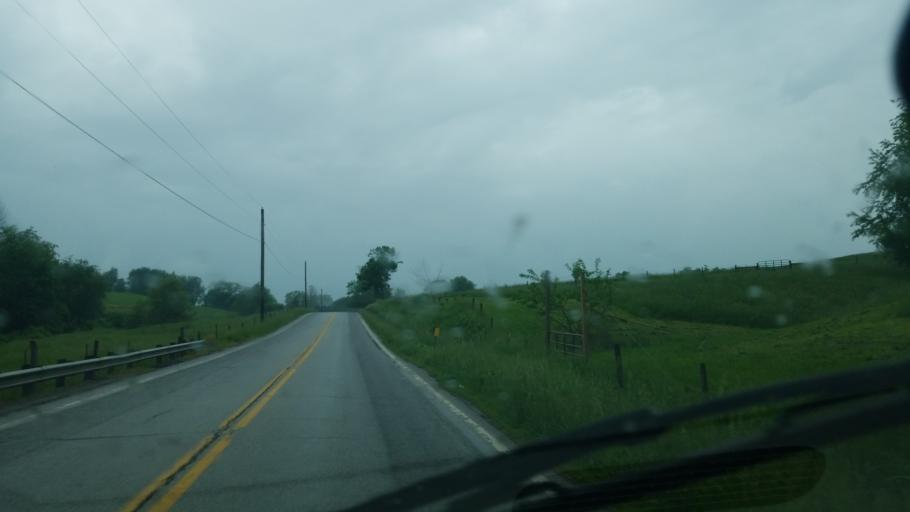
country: US
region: Ohio
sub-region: Tuscarawas County
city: Sugarcreek
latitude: 40.4891
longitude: -81.7523
